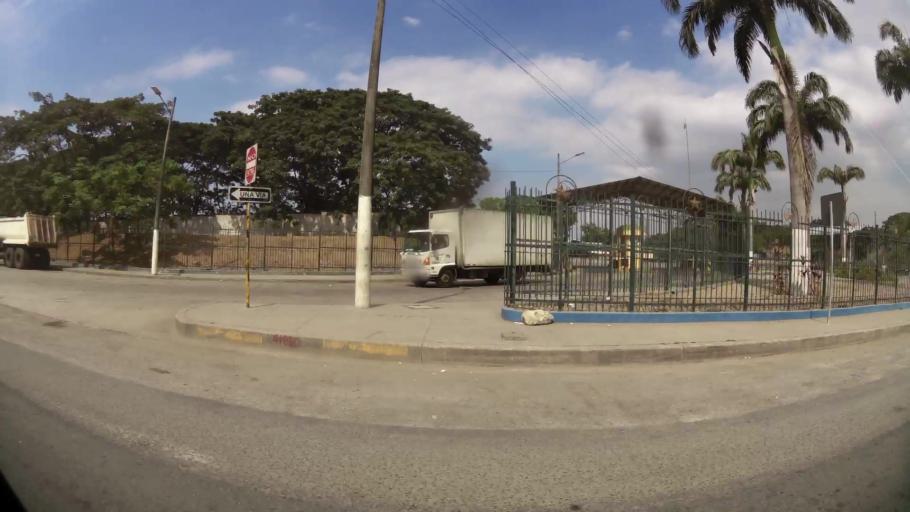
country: EC
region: Guayas
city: Santa Lucia
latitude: -2.0878
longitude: -79.9471
